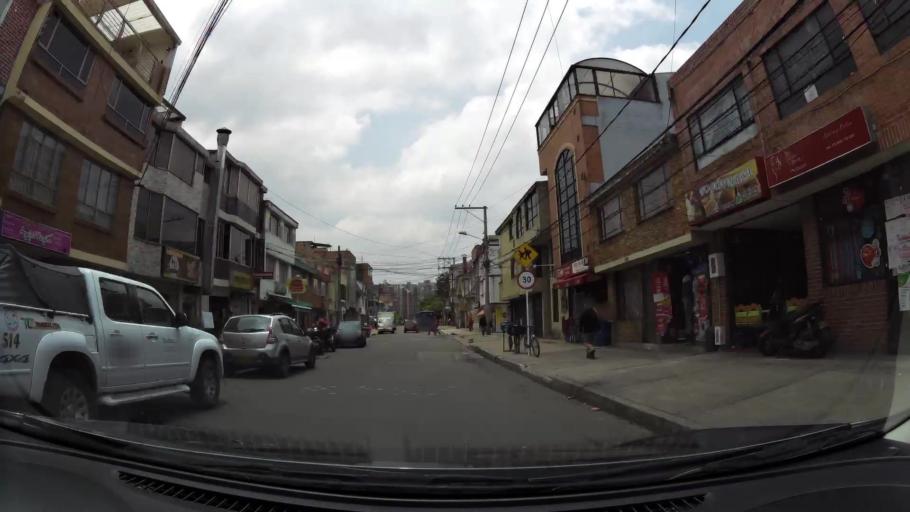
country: CO
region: Cundinamarca
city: Cota
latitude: 4.7468
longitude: -74.0627
